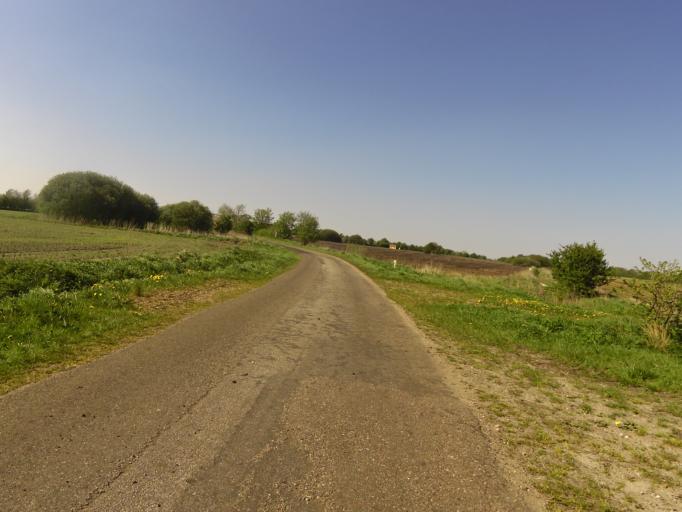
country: DK
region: South Denmark
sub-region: Tonder Kommune
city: Sherrebek
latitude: 55.2111
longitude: 8.8436
